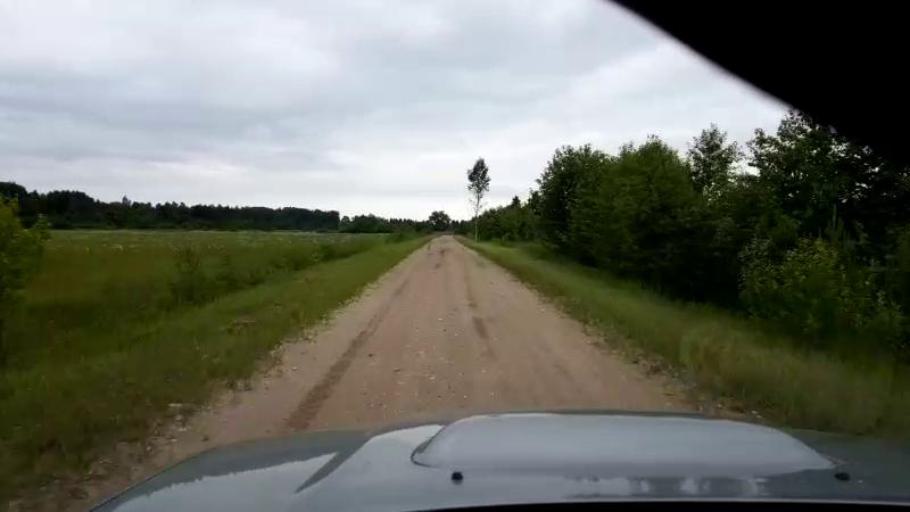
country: EE
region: Paernumaa
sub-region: Halinga vald
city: Parnu-Jaagupi
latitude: 58.5532
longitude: 24.5740
